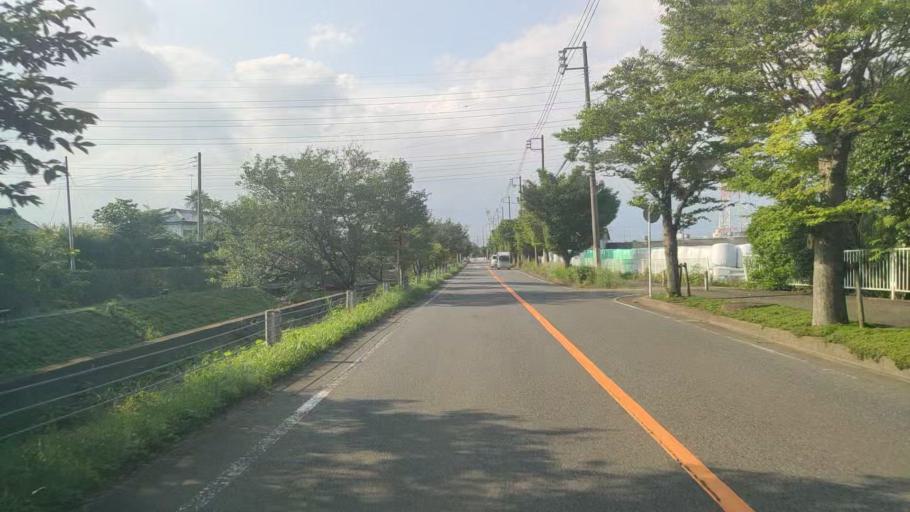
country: JP
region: Kanagawa
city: Isehara
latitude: 35.3963
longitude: 139.3380
